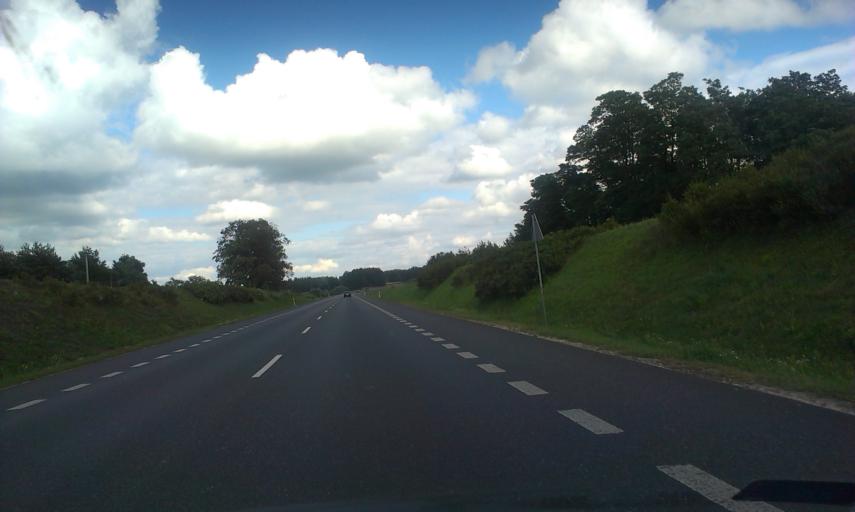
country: PL
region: Masovian Voivodeship
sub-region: Powiat zyrardowski
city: Radziejowice
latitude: 51.9786
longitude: 20.5584
